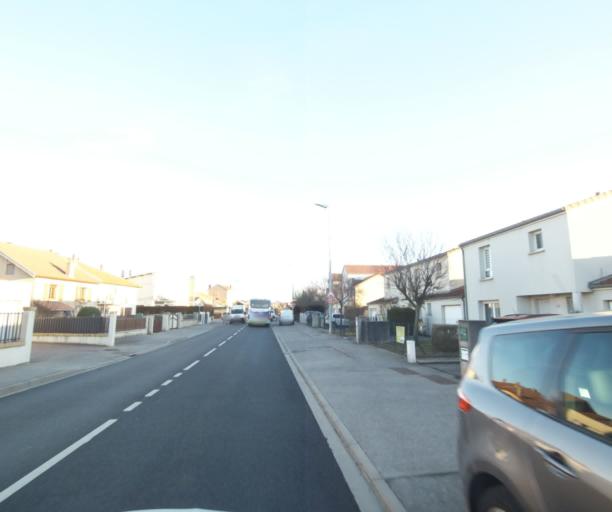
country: FR
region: Lorraine
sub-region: Departement de Meurthe-et-Moselle
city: Tomblaine
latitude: 48.6789
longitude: 6.2178
